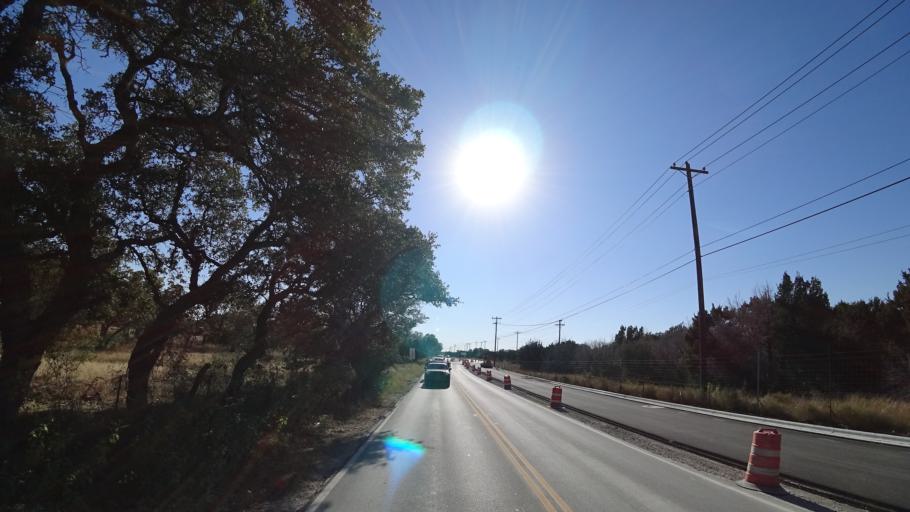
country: US
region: Texas
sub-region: Williamson County
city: Cedar Park
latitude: 30.4940
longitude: -97.8589
